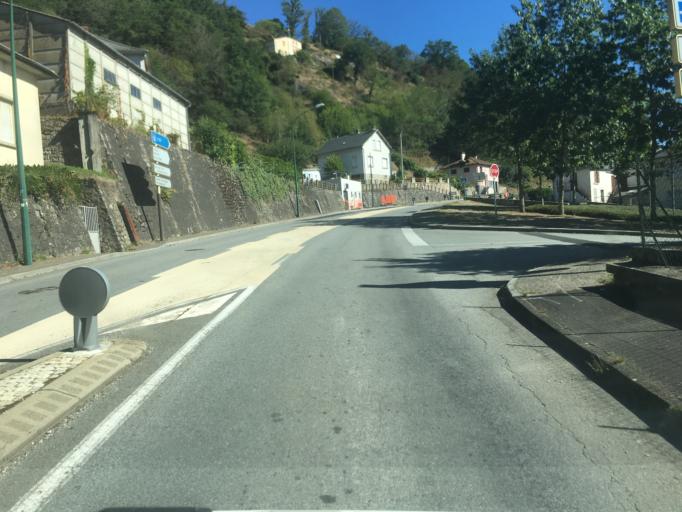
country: FR
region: Limousin
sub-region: Departement de la Correze
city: Bort-les-Orgues
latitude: 45.4019
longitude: 2.4939
